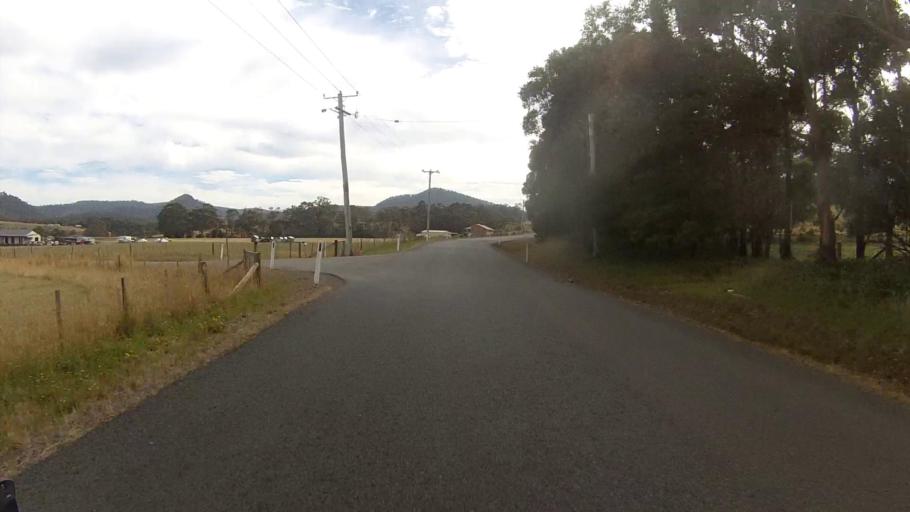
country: AU
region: Tasmania
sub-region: Sorell
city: Sorell
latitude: -42.7911
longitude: 147.7999
